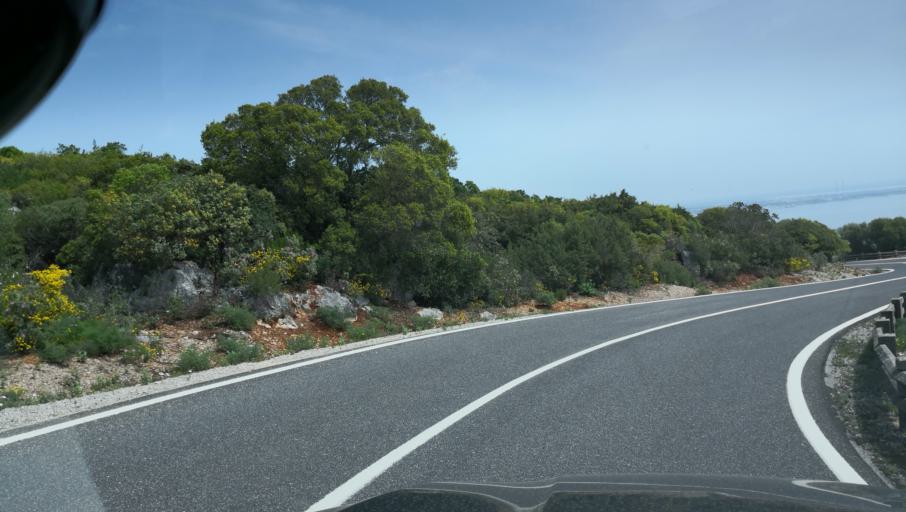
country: PT
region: Setubal
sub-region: Setubal
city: Setubal
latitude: 38.4904
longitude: -8.9397
